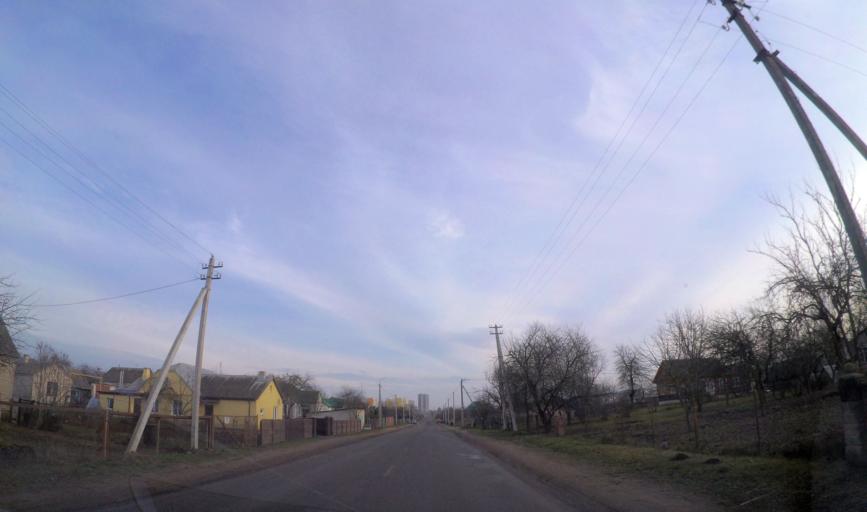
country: BY
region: Grodnenskaya
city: Hrodna
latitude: 53.7190
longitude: 23.8513
